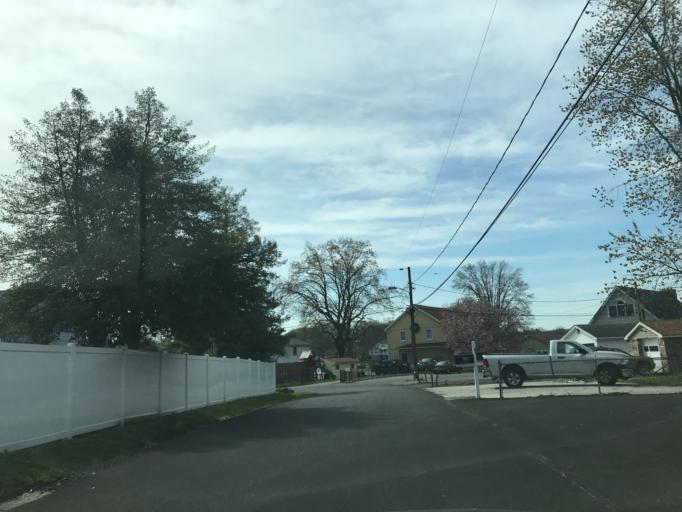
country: US
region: Maryland
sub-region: Baltimore County
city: Middle River
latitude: 39.3059
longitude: -76.4265
